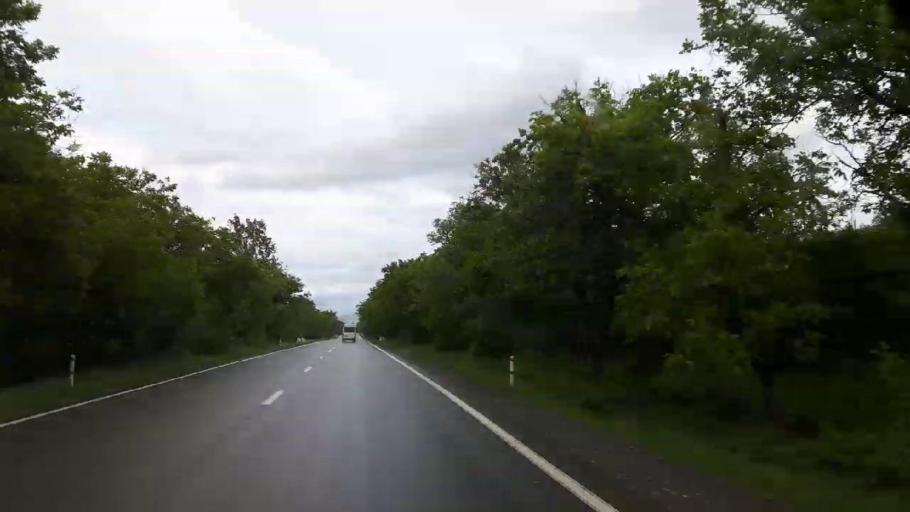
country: GE
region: Shida Kartli
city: Kaspi
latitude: 41.9559
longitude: 44.4899
